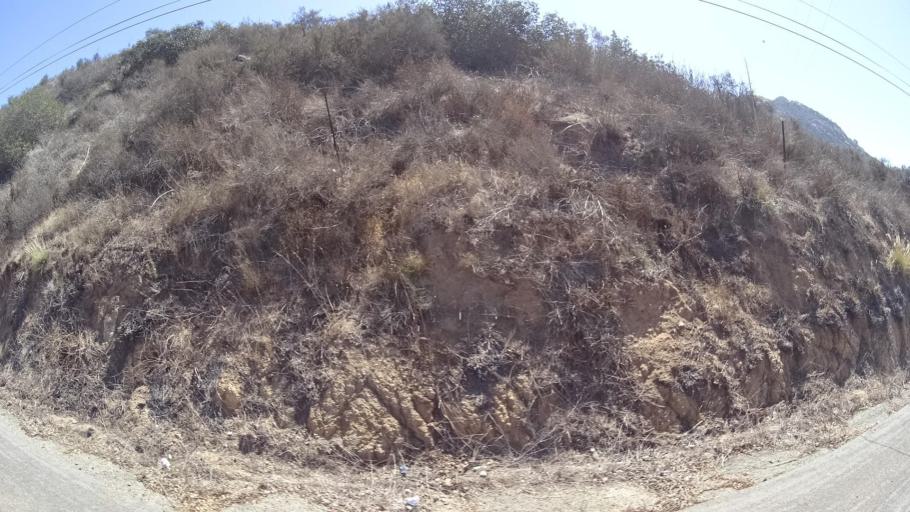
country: US
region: California
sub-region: San Diego County
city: Rainbow
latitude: 33.4294
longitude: -117.1412
